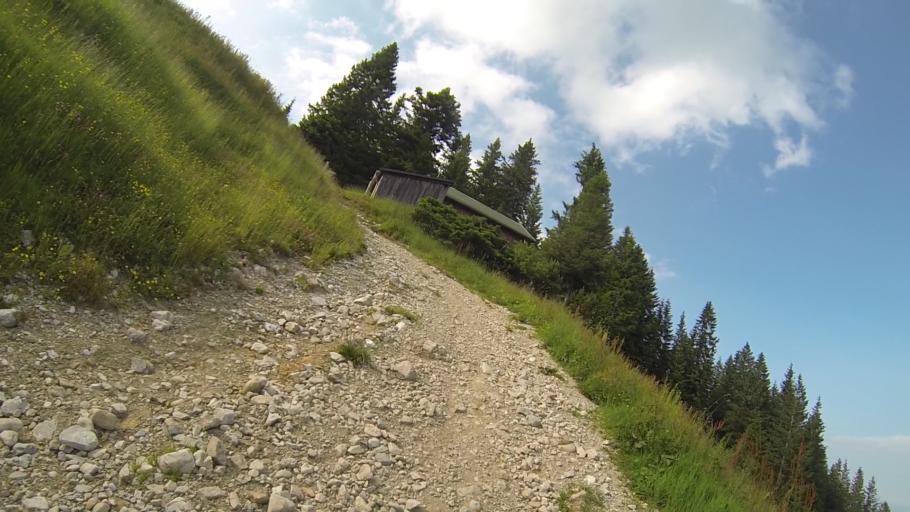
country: DE
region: Bavaria
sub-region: Swabia
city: Nesselwang
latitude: 47.5919
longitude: 10.5009
